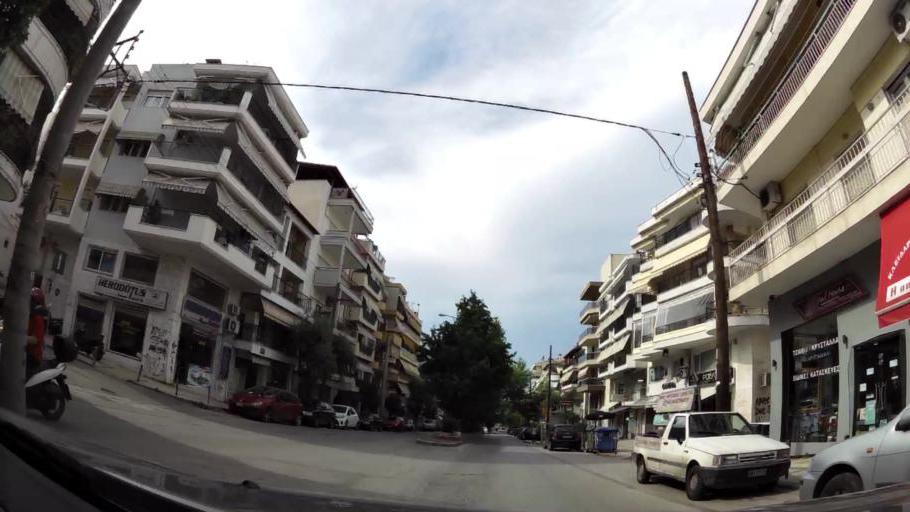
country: GR
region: Central Macedonia
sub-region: Nomos Thessalonikis
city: Kalamaria
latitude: 40.5824
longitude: 22.9532
